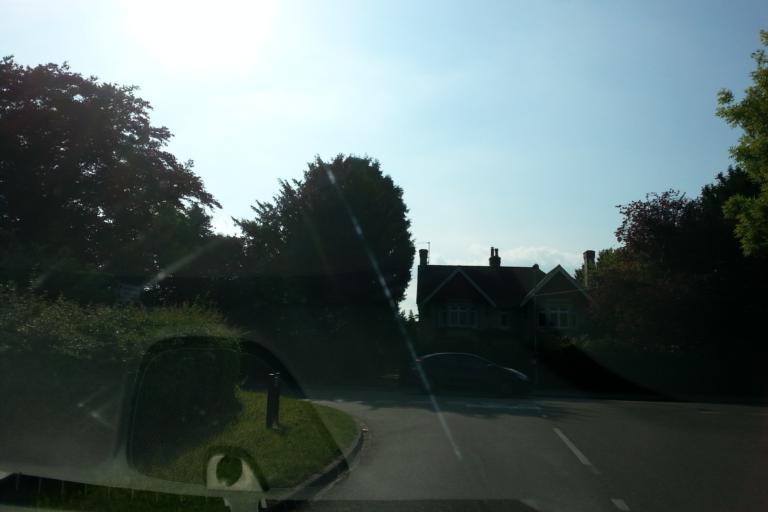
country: GB
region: England
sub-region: Cambridgeshire
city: Swavesey
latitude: 52.3129
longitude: 0.0077
